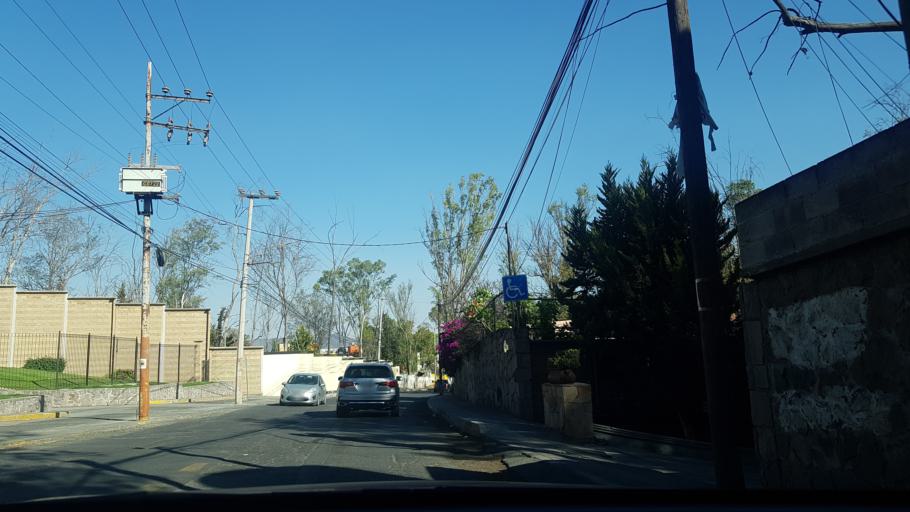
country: MX
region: Mexico
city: Cuautitlan Izcalli
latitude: 19.6258
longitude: -99.2340
